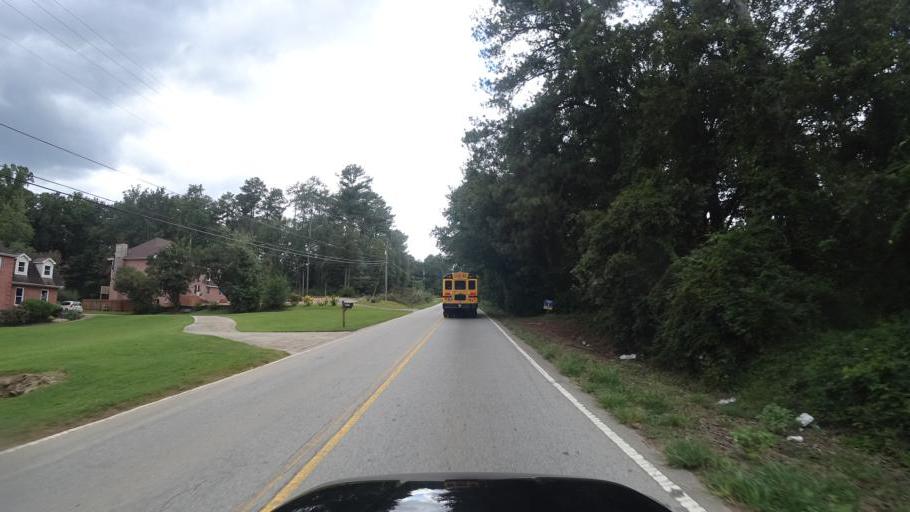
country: US
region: Georgia
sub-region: DeKalb County
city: Panthersville
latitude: 33.6566
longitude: -84.2375
